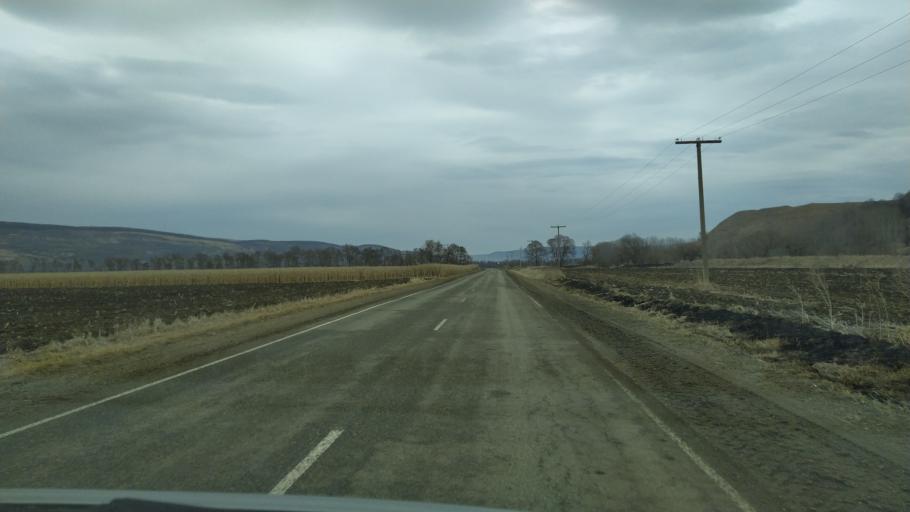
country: RU
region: Krasnodarskiy
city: Peredovaya
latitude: 44.1021
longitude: 41.4118
